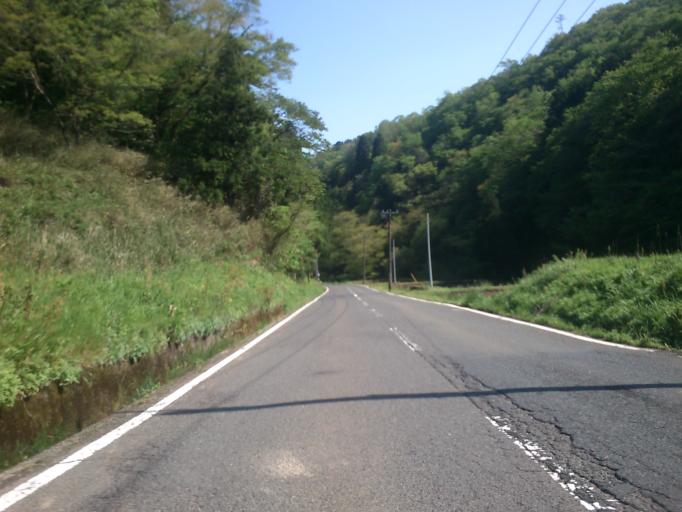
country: JP
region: Kyoto
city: Miyazu
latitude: 35.6254
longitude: 135.1260
